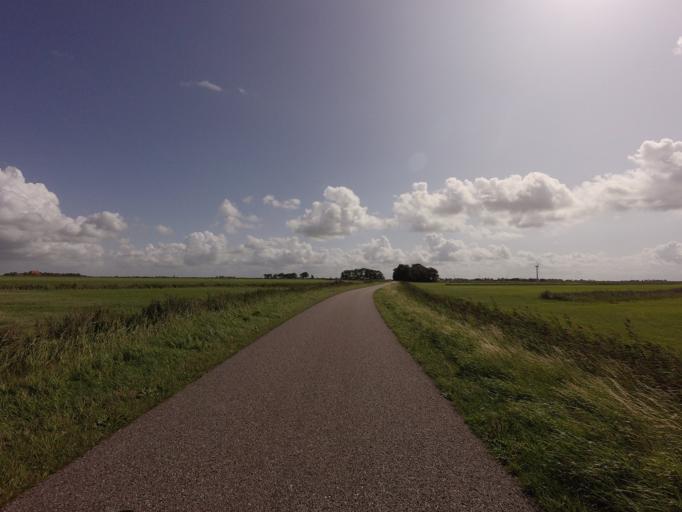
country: NL
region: Friesland
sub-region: Sudwest Fryslan
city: Makkum
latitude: 53.0656
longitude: 5.4434
